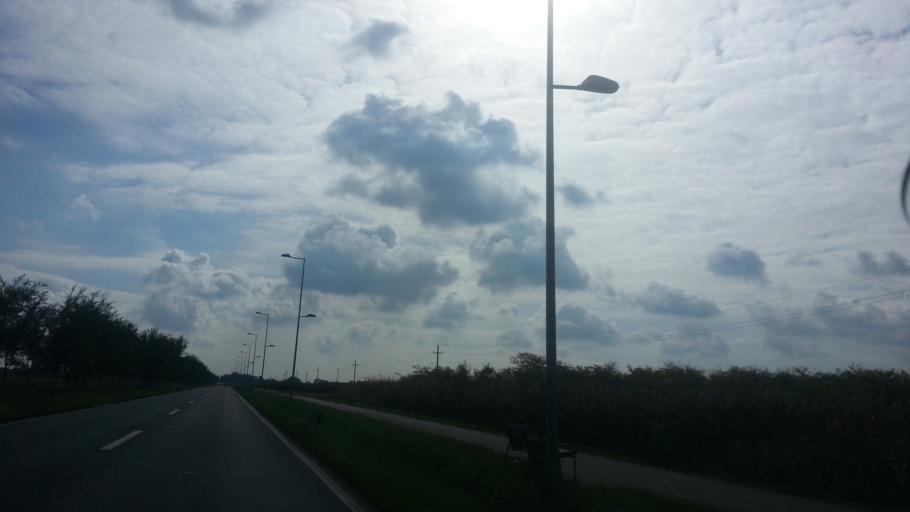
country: RS
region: Autonomna Pokrajina Vojvodina
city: Nova Pazova
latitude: 44.9625
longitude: 20.1911
